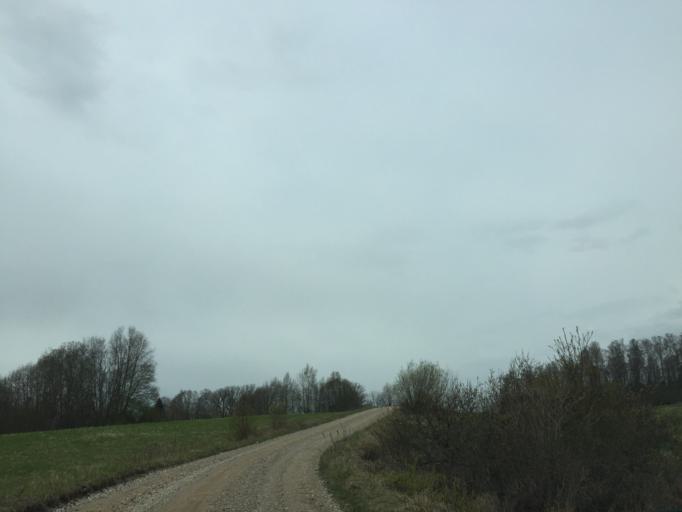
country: LV
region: Amatas Novads
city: Drabesi
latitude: 57.2598
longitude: 25.3064
